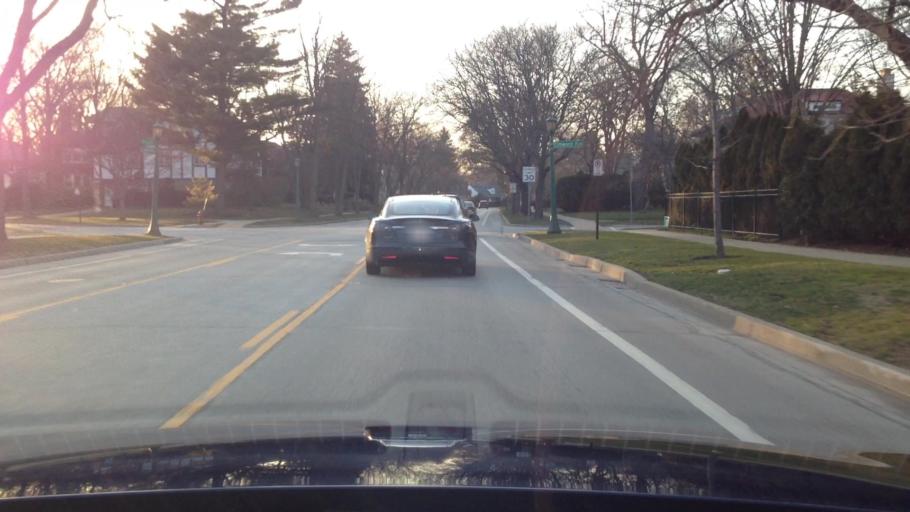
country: US
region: Illinois
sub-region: Cook County
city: Kenilworth
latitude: 42.0812
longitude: -87.6949
